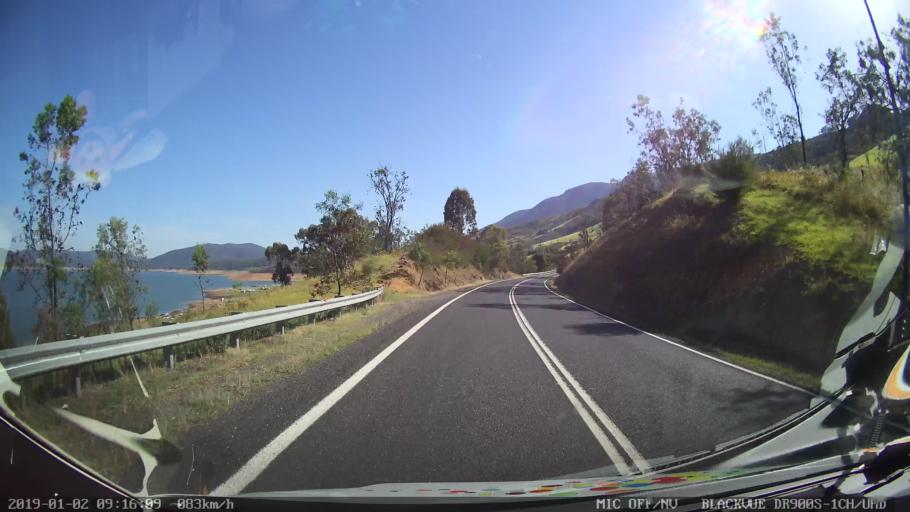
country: AU
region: New South Wales
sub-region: Tumut Shire
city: Tumut
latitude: -35.4564
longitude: 148.2820
